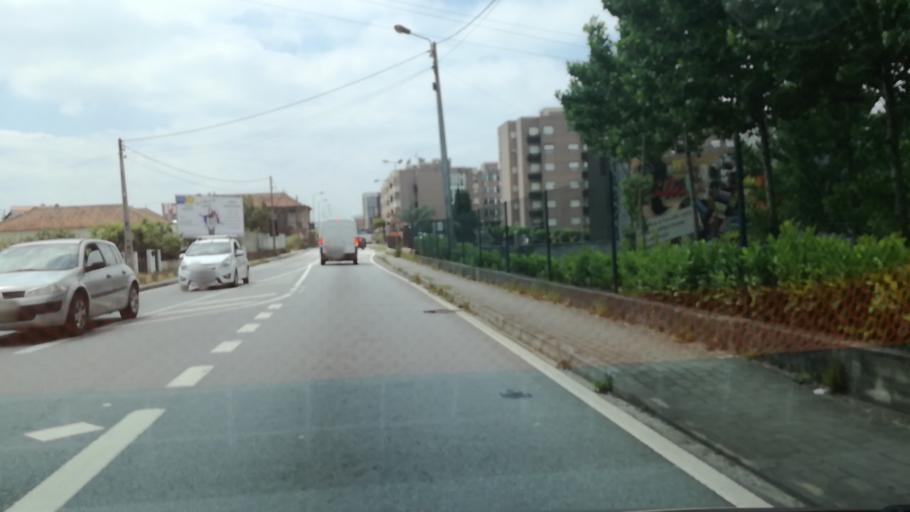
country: PT
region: Braga
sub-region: Vila Nova de Famalicao
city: Ferreiros
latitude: 41.3537
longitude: -8.5535
